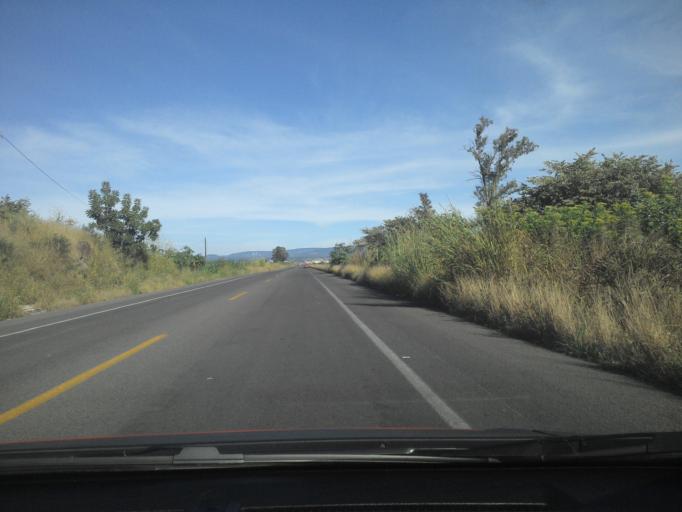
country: MX
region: Jalisco
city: El Refugio
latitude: 20.6655
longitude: -103.7729
